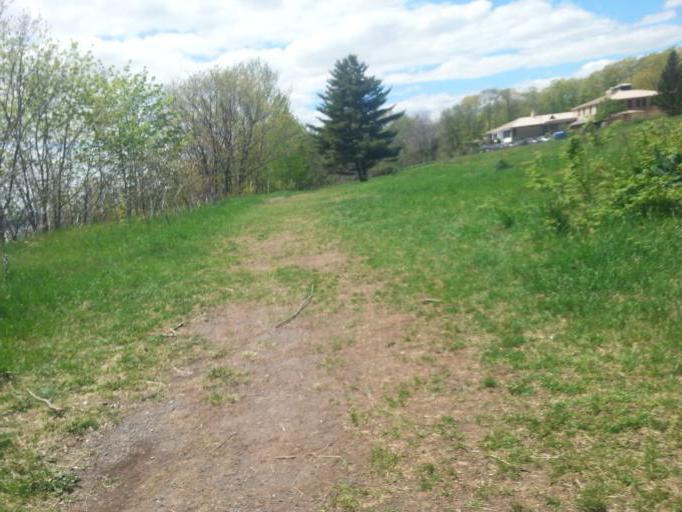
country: CA
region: Quebec
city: Quebec
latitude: 46.7734
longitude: -71.2493
